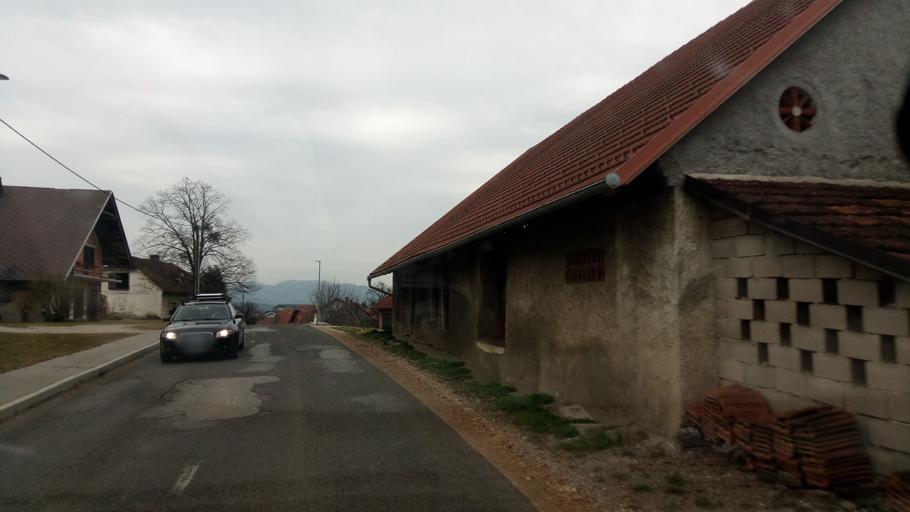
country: SI
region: Slovenska Konjice
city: Slovenske Konjice
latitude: 46.3307
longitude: 15.4790
